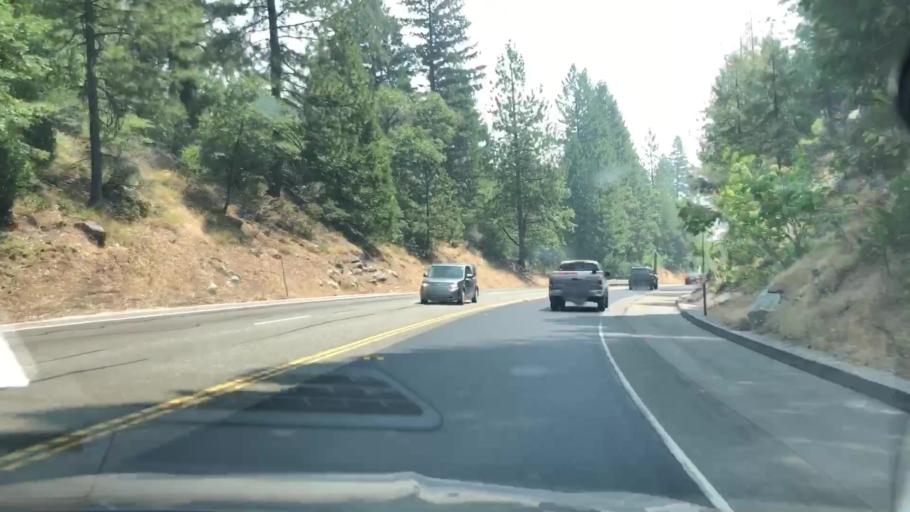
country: US
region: California
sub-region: El Dorado County
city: Pollock Pines
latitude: 38.7632
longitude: -120.5437
